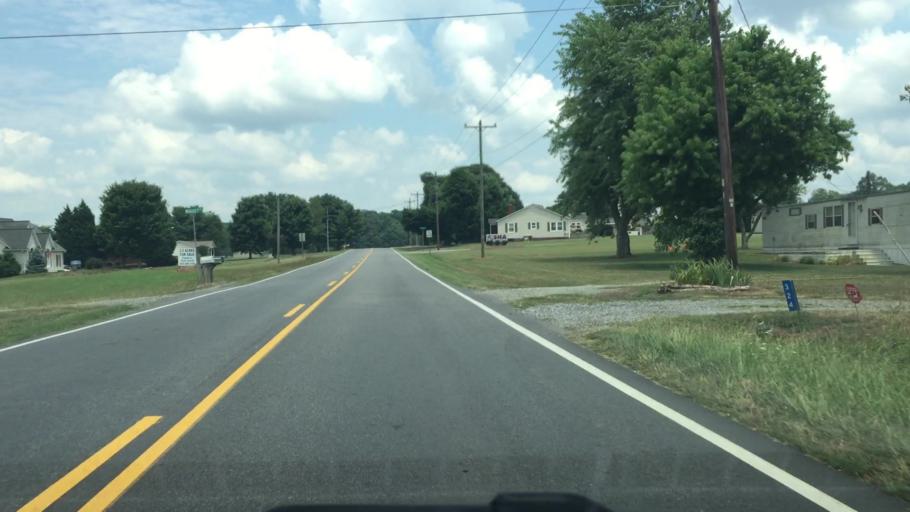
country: US
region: North Carolina
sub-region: Iredell County
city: Troutman
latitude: 35.7182
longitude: -80.8819
